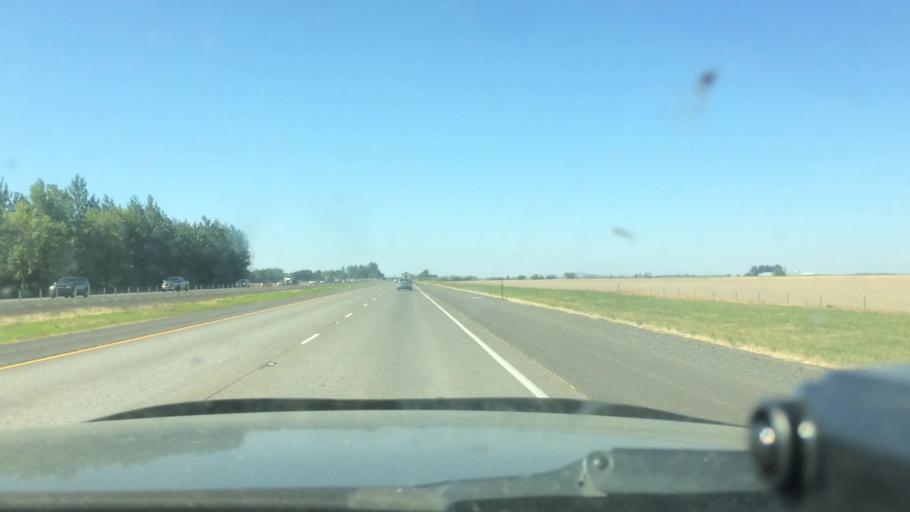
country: US
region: Oregon
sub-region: Linn County
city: Tangent
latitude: 44.4907
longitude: -123.0615
